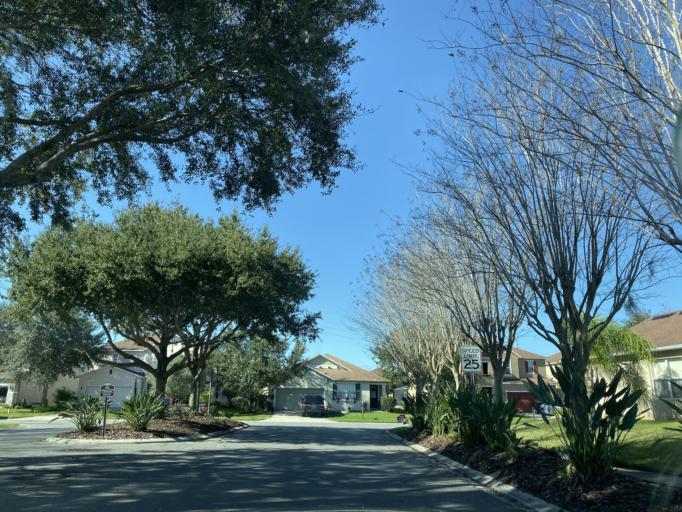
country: US
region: Florida
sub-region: Orange County
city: Meadow Woods
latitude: 28.3985
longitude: -81.2423
